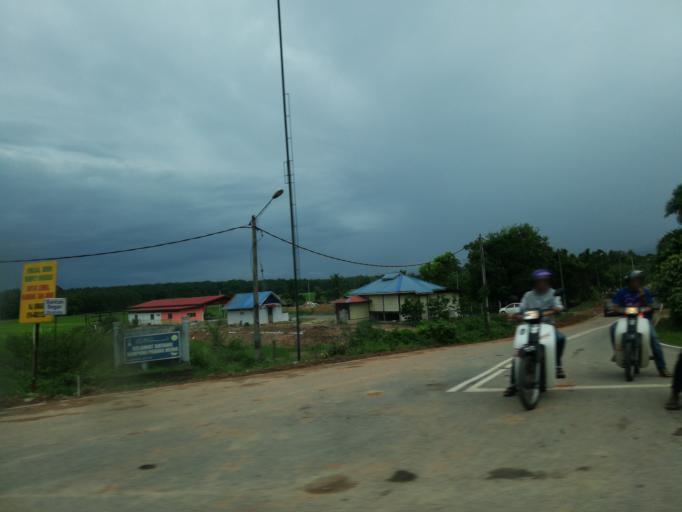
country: MY
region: Penang
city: Tasek Glugor
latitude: 5.5006
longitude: 100.6135
